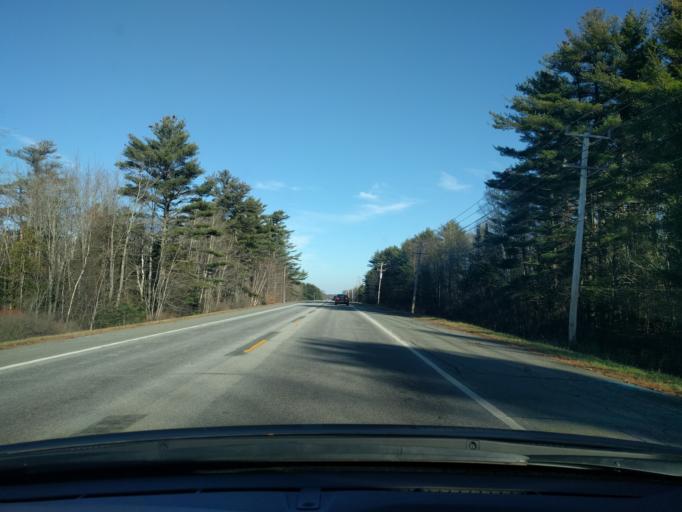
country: US
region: Maine
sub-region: Penobscot County
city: Hampden
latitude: 44.7663
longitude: -68.8155
